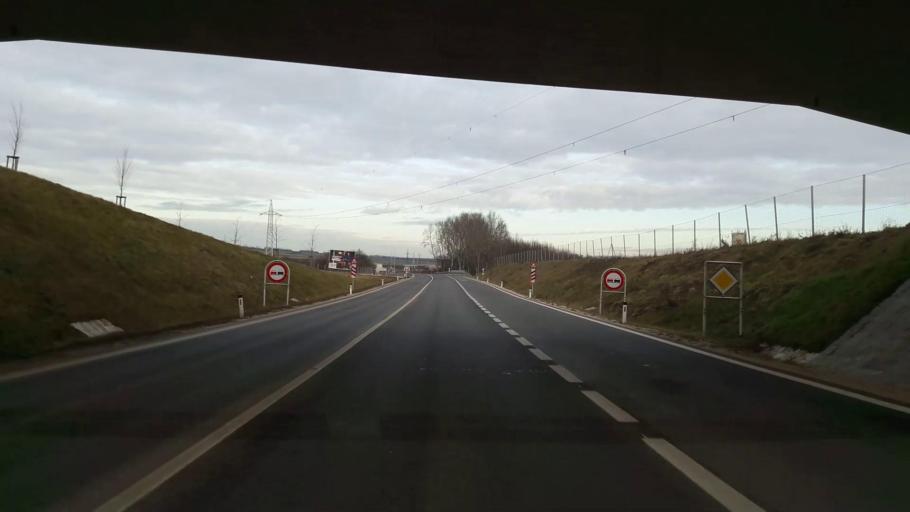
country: AT
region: Lower Austria
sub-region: Politischer Bezirk Mistelbach
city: Mistelbach
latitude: 48.5544
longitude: 16.5588
